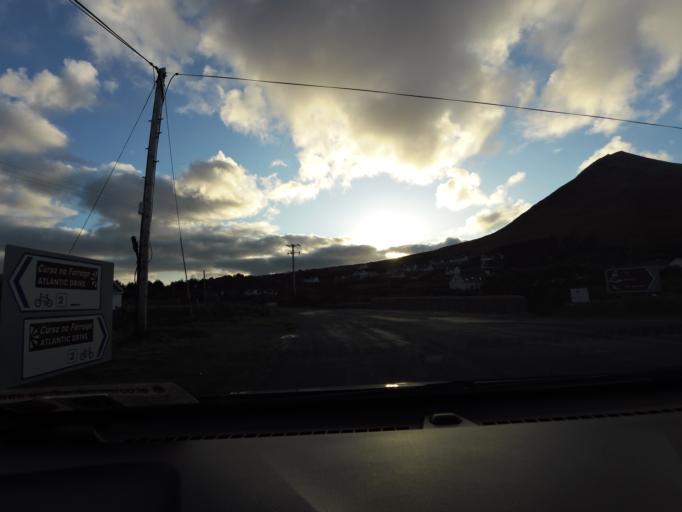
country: IE
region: Connaught
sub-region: Maigh Eo
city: Belmullet
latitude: 54.0097
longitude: -10.0248
